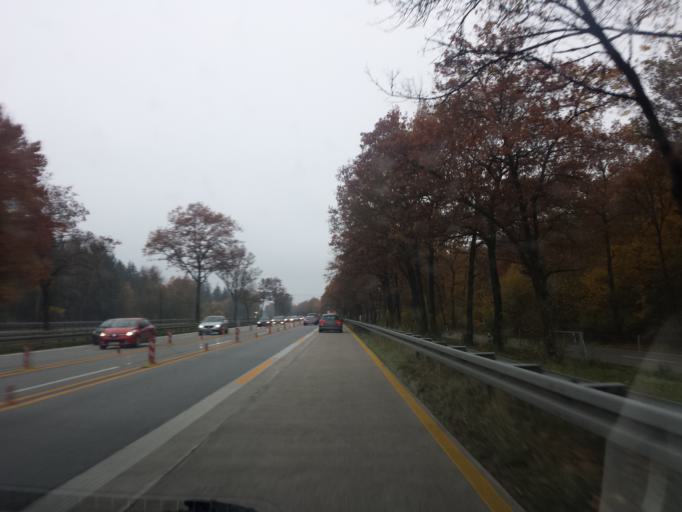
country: DE
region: Bavaria
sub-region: Upper Bavaria
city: Neuried
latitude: 48.0563
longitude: 11.4626
